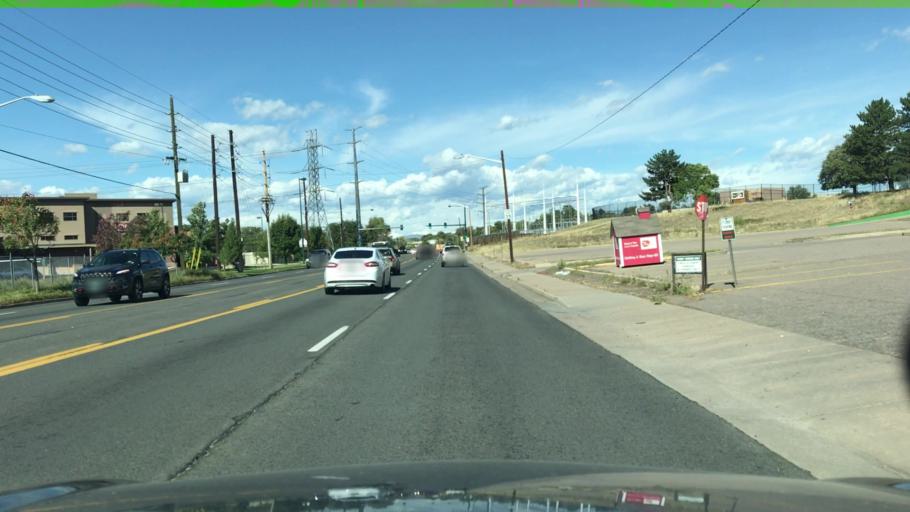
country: US
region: Colorado
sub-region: Arapahoe County
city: Glendale
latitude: 39.7043
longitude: -104.9155
